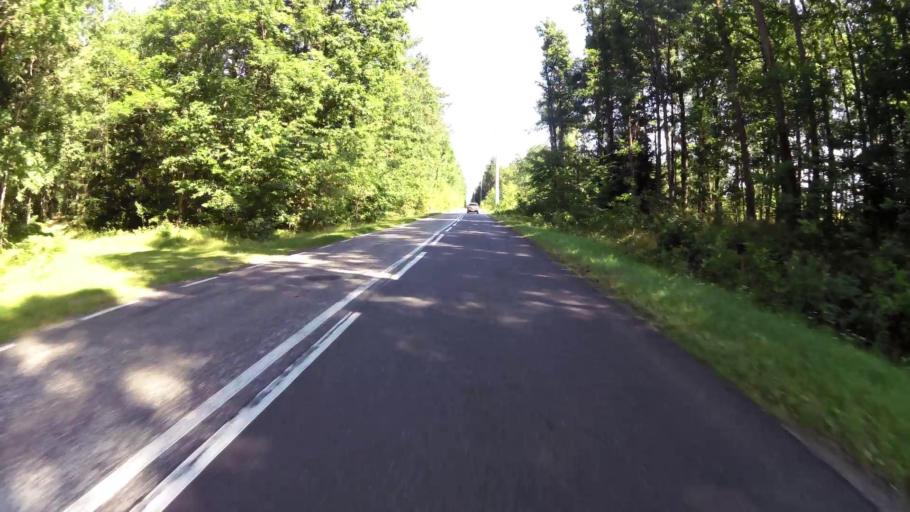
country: PL
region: West Pomeranian Voivodeship
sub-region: Powiat drawski
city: Czaplinek
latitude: 53.4474
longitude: 16.2122
